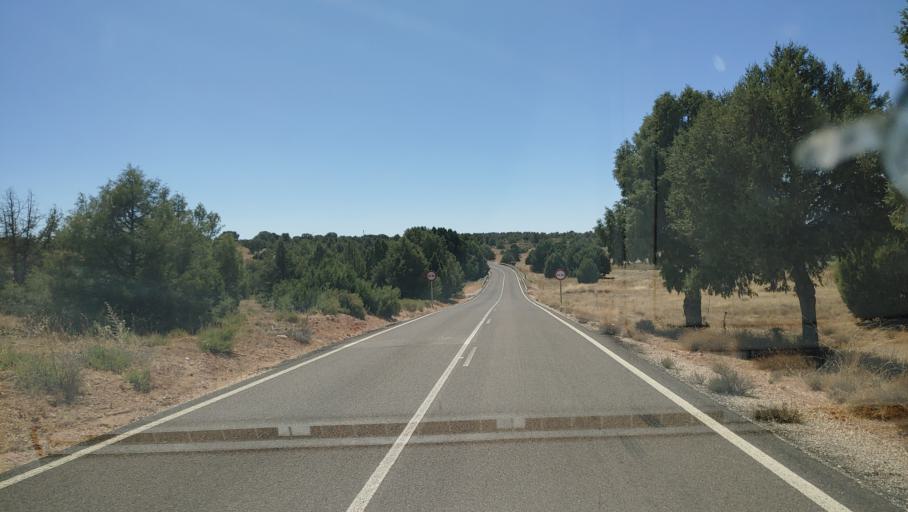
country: ES
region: Castille-La Mancha
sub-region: Provincia de Albacete
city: Ossa de Montiel
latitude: 38.8661
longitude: -2.7981
